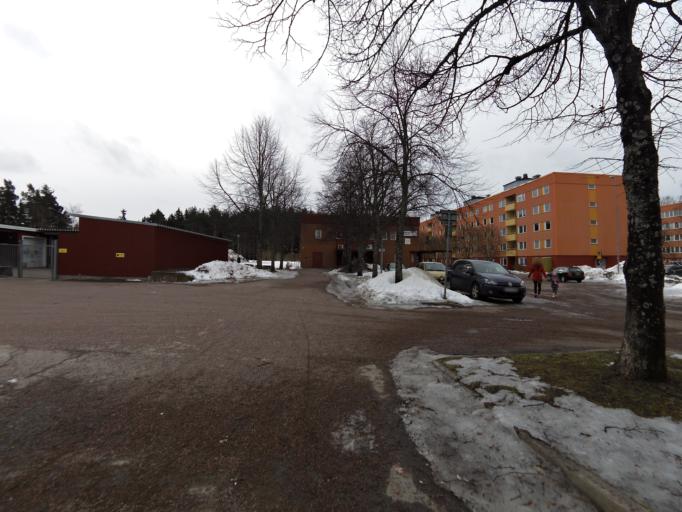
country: SE
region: Gaevleborg
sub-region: Gavle Kommun
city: Gavle
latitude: 60.6508
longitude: 17.1377
